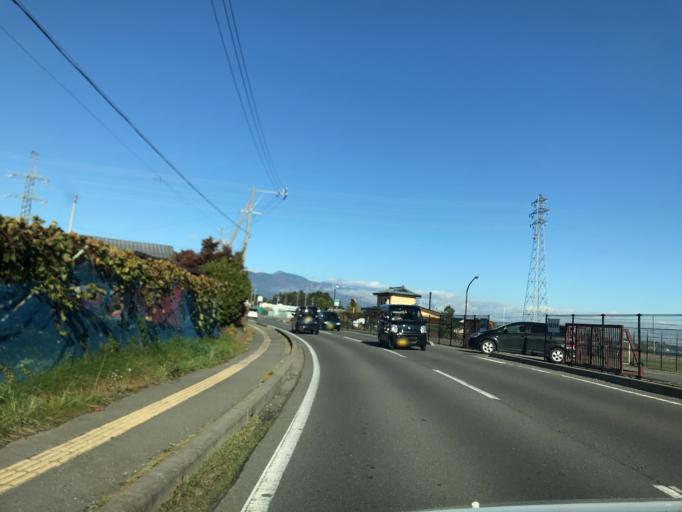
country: JP
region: Nagano
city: Shiojiri
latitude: 36.1274
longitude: 137.9375
